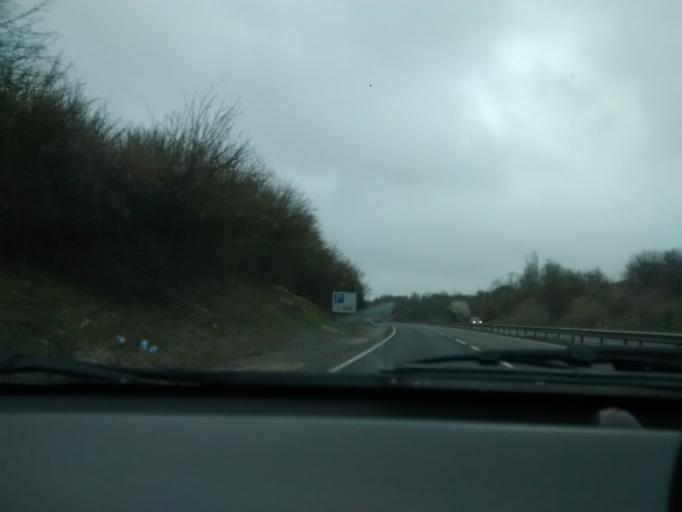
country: GB
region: England
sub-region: Suffolk
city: Needham Market
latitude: 52.1743
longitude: 1.0512
